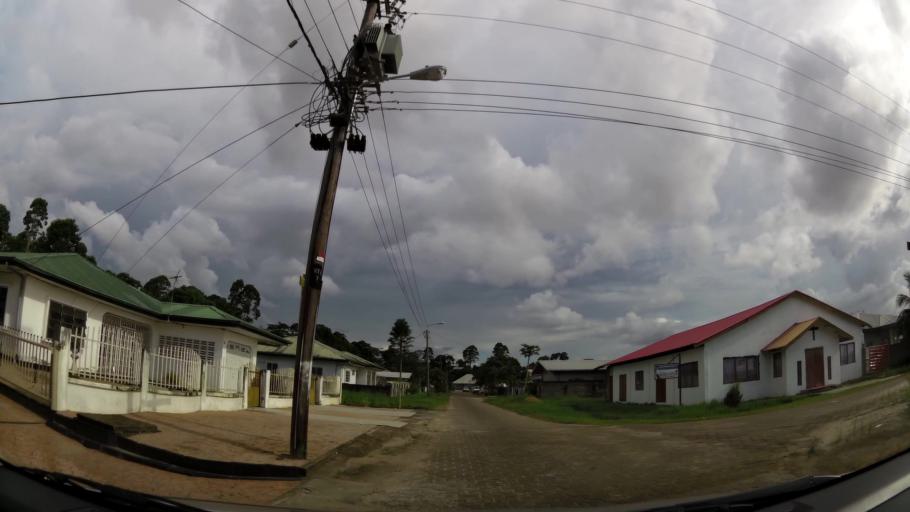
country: SR
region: Paramaribo
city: Paramaribo
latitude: 5.8561
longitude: -55.1775
